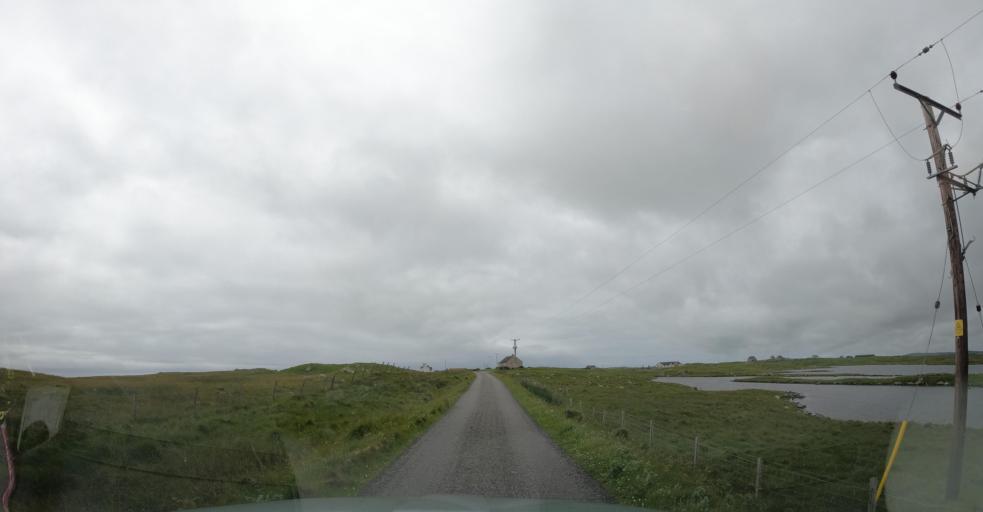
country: GB
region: Scotland
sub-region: Eilean Siar
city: Isle of North Uist
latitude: 57.5423
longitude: -7.3347
